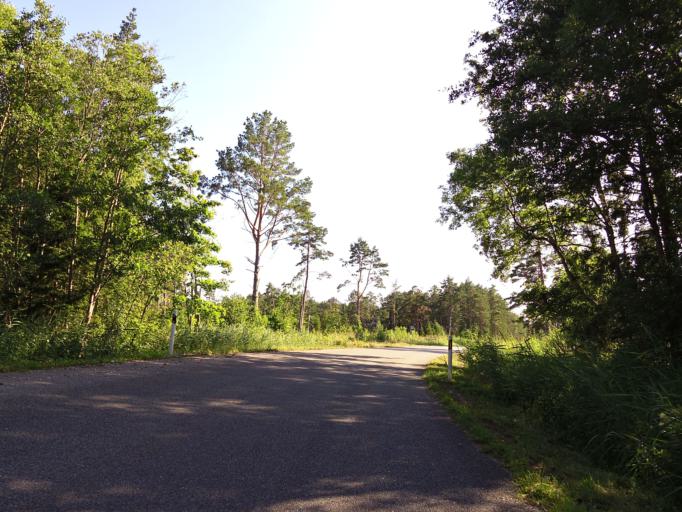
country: EE
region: Hiiumaa
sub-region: Kaerdla linn
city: Kardla
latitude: 58.8984
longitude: 22.2793
